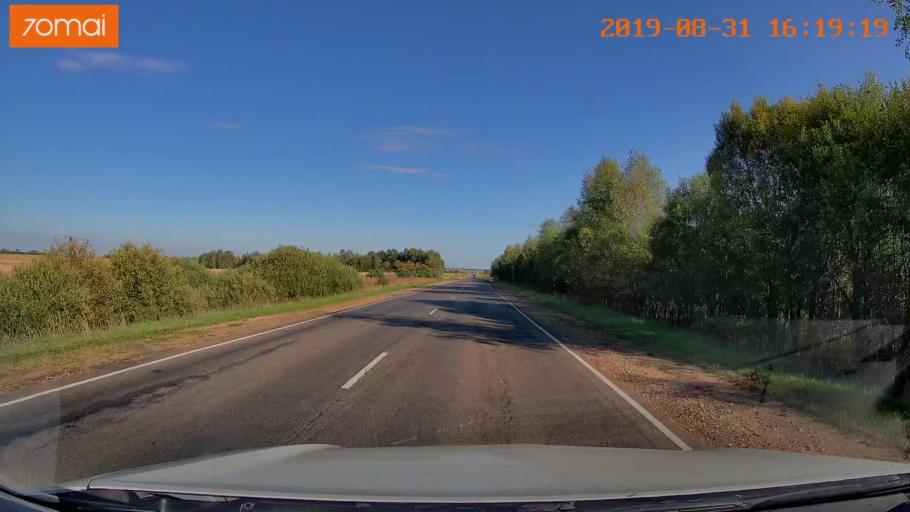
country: RU
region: Kaluga
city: Nikola-Lenivets
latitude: 54.5300
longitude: 35.5756
